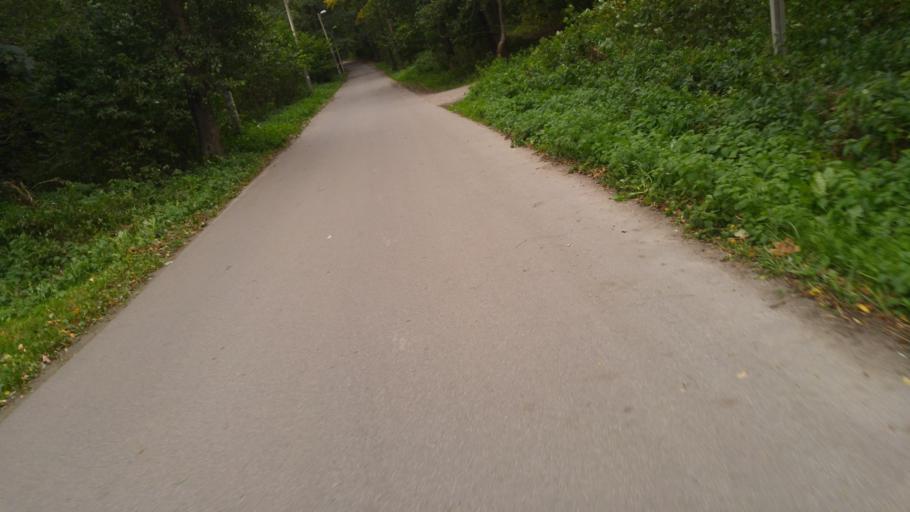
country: RU
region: Kaliningrad
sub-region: Gorod Kaliningrad
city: Kaliningrad
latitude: 54.7282
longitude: 20.4515
